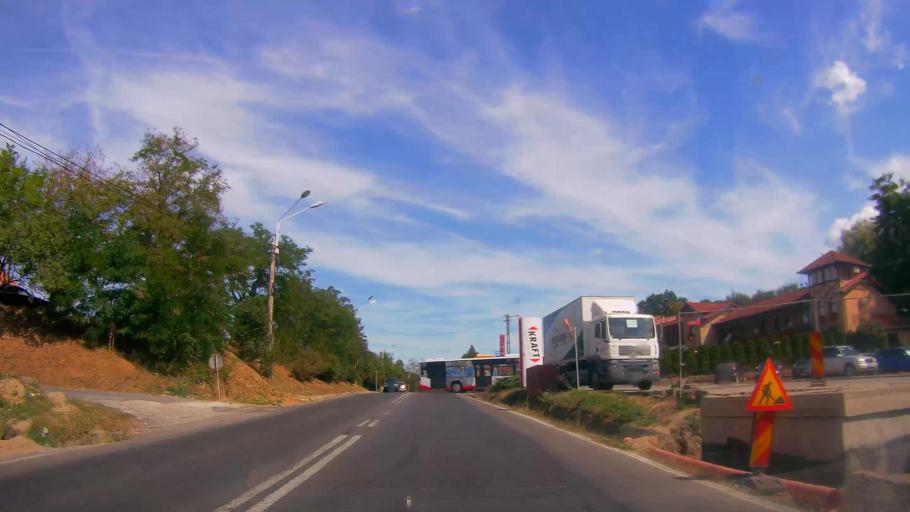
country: RO
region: Mures
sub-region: Municipiul Sighisoara
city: Sighisoara
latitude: 46.2248
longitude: 24.7756
